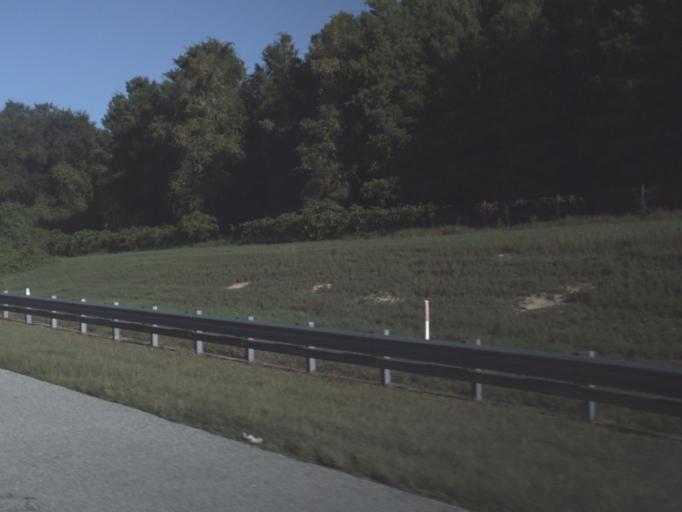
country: US
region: Florida
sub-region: Lake County
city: Howie In The Hills
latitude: 28.6624
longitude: -81.8275
